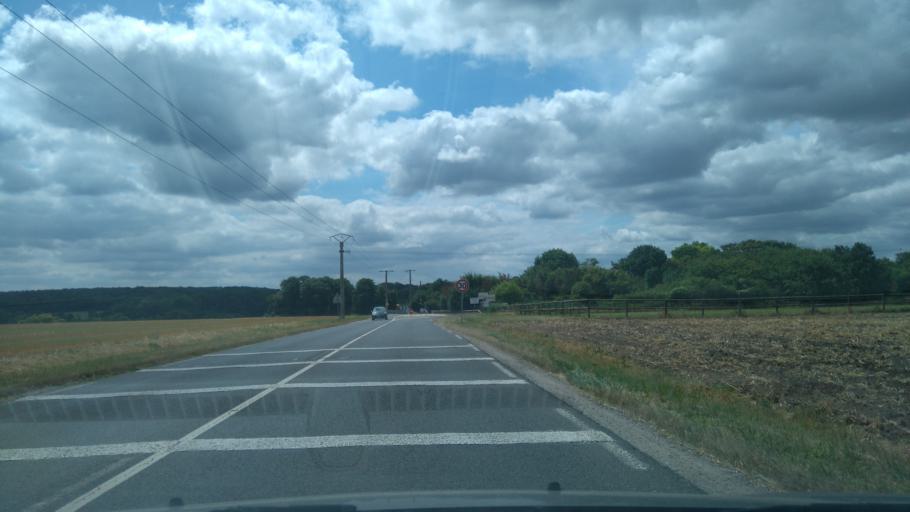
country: FR
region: Picardie
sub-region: Departement de l'Oise
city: Gouvieux
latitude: 49.2010
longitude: 2.4357
